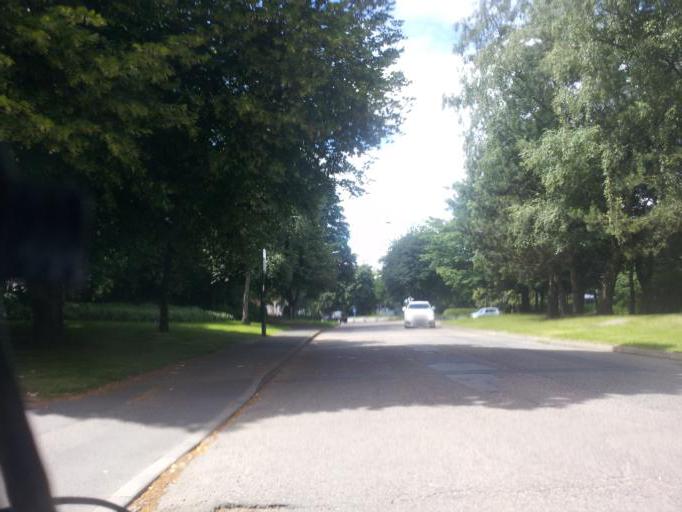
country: GB
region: England
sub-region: Kent
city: Kings Hill
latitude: 51.2738
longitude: 0.3952
